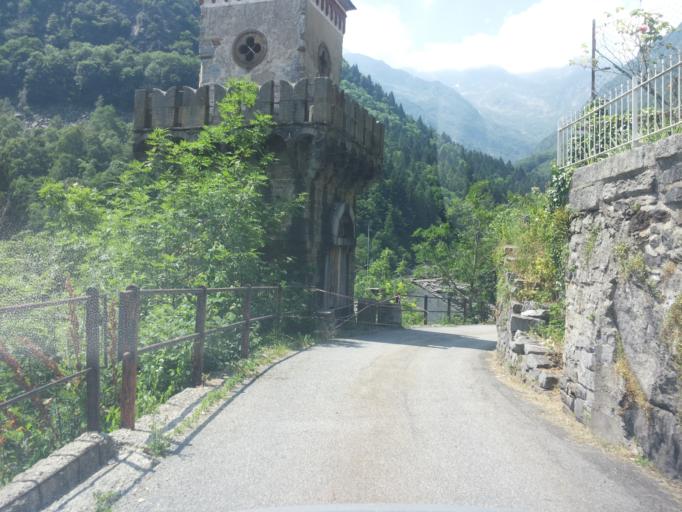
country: IT
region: Piedmont
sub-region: Provincia di Biella
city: Rosazza
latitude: 45.6751
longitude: 7.9746
